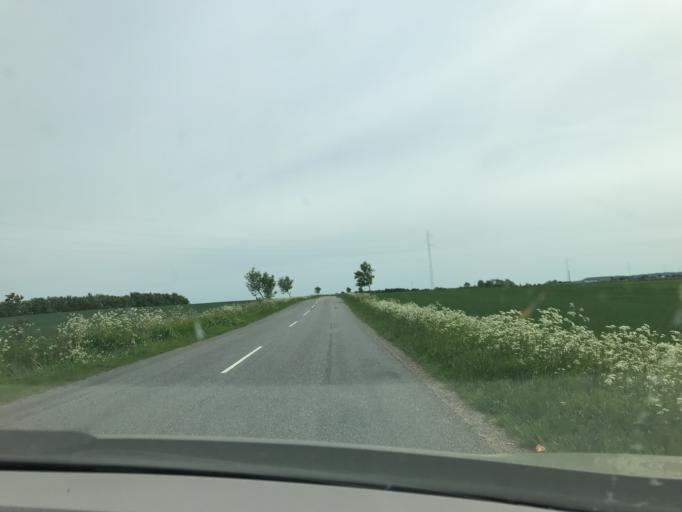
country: DK
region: Central Jutland
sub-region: Norddjurs Kommune
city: Allingabro
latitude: 56.5181
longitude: 10.3280
